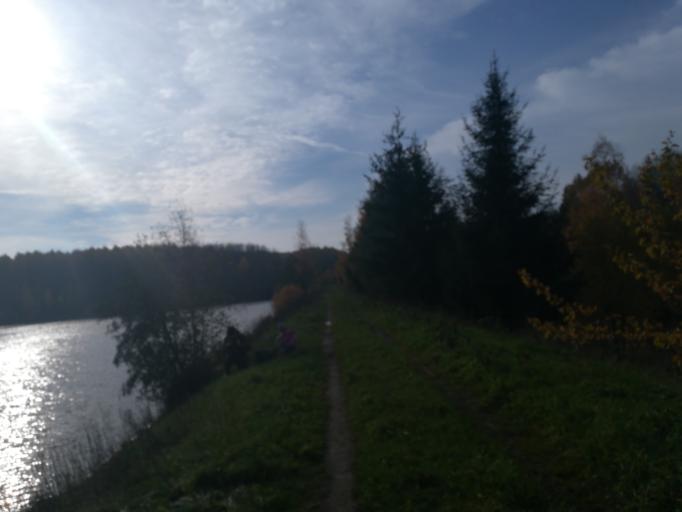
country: RU
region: Leningrad
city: Sista-Palkino
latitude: 59.5913
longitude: 28.8271
